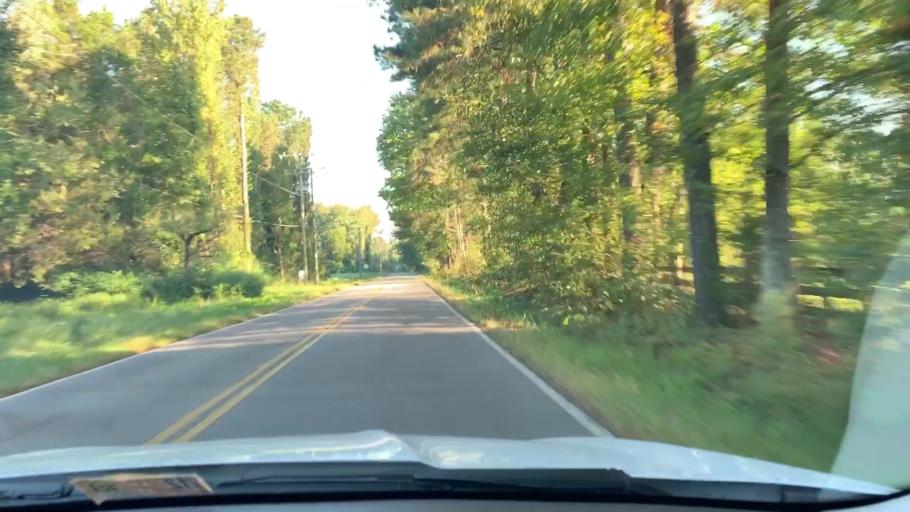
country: US
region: Virginia
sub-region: Middlesex County
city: Deltaville
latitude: 37.5551
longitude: -76.4515
